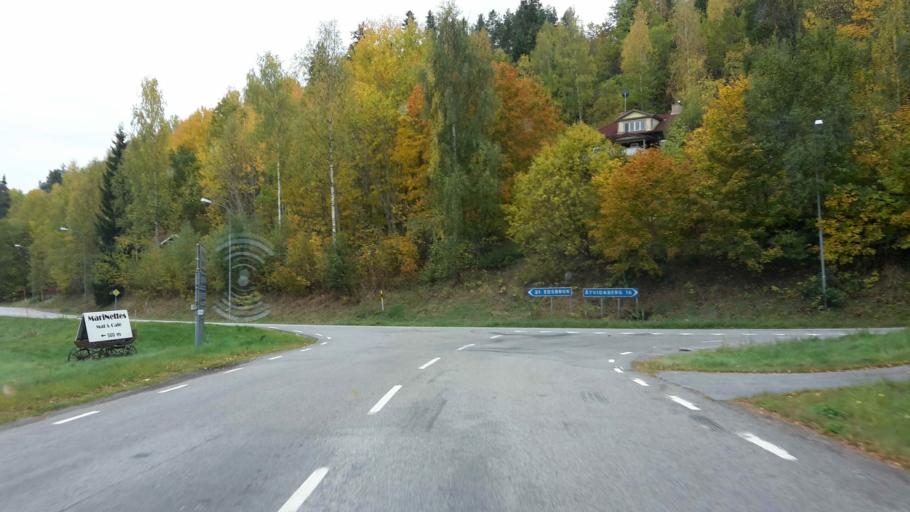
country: SE
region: Kalmar
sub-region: Vasterviks Kommun
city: Overum
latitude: 58.1427
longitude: 16.2094
